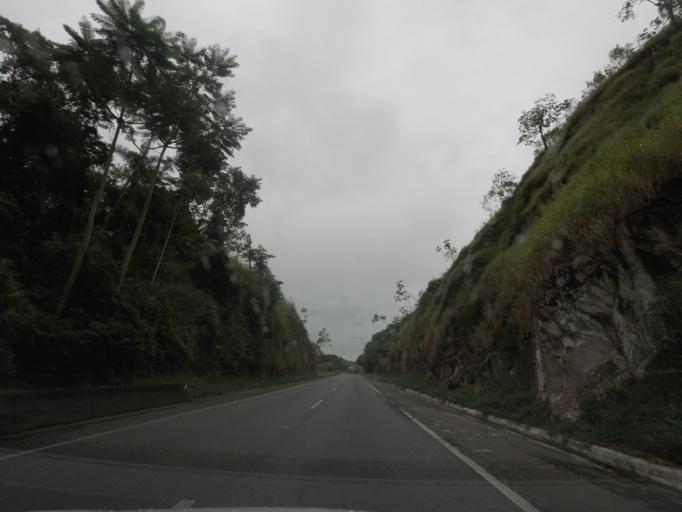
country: BR
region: Sao Paulo
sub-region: Cajati
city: Cajati
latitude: -24.7960
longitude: -48.2082
